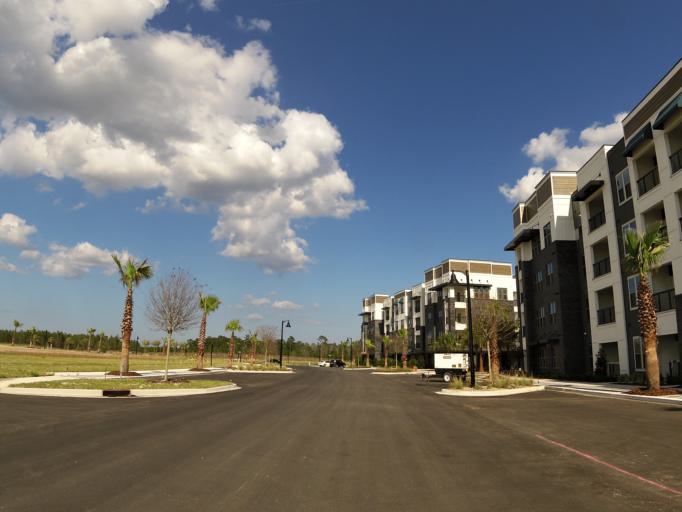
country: US
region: Florida
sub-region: Saint Johns County
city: Palm Valley
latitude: 30.1651
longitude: -81.5084
